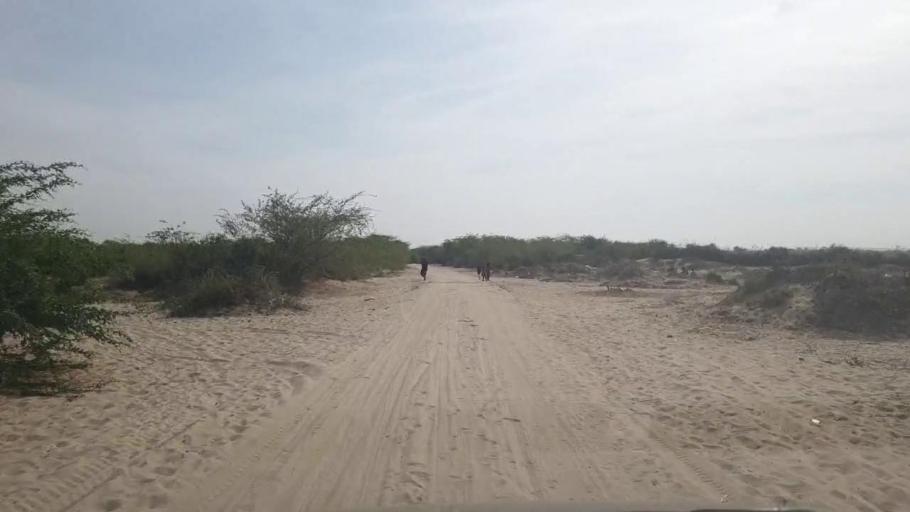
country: PK
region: Sindh
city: Umarkot
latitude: 25.2939
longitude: 69.7302
